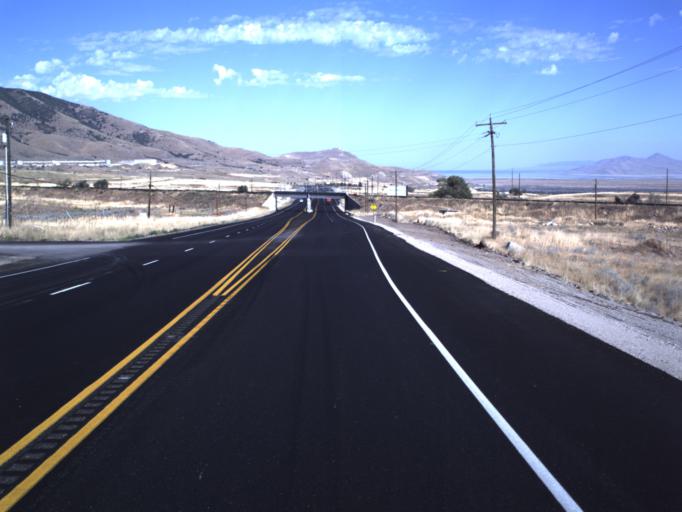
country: US
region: Utah
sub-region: Salt Lake County
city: Oquirrh
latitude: 40.6495
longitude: -112.0711
